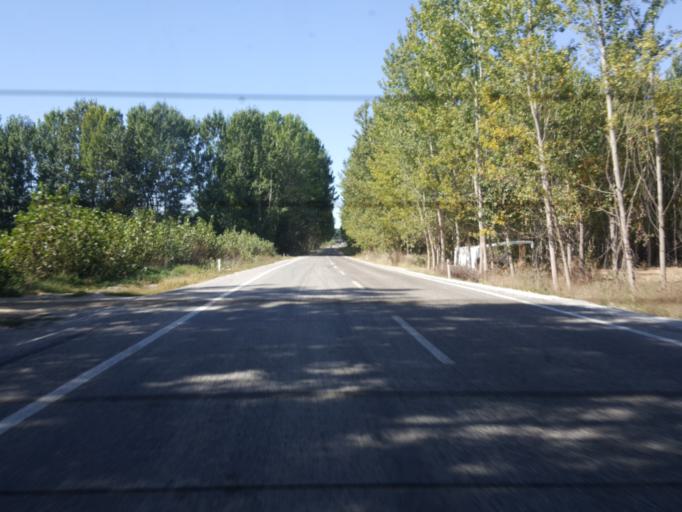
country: TR
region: Tokat
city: Pazar
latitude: 40.2682
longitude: 36.2091
